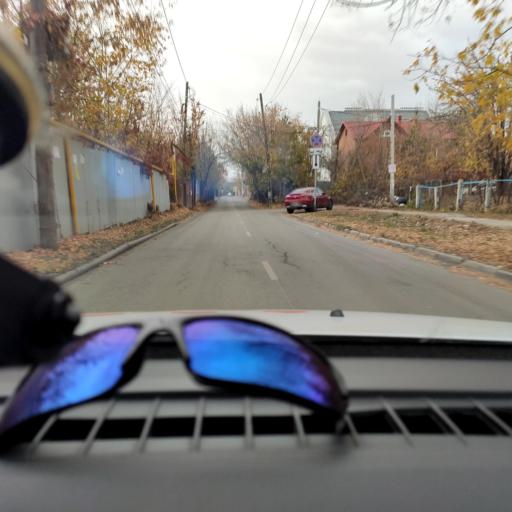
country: RU
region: Samara
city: Samara
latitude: 53.2348
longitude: 50.1774
